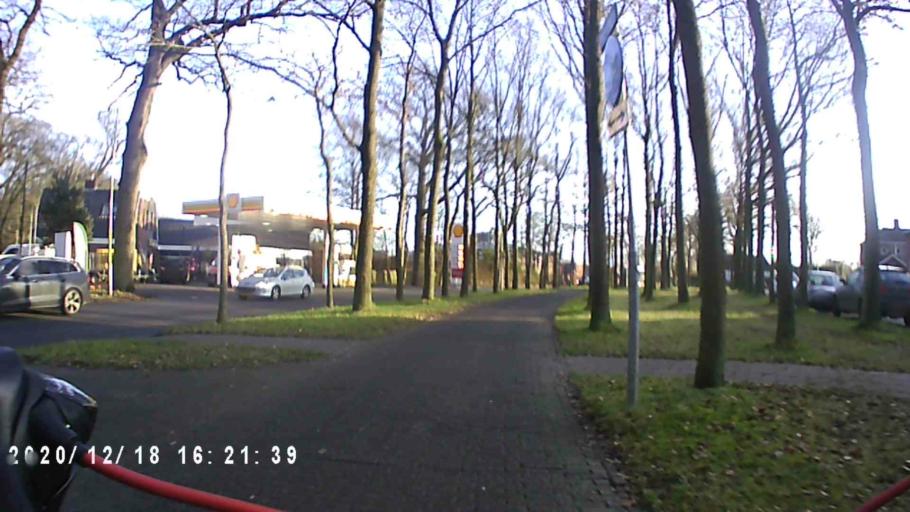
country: NL
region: Drenthe
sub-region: Gemeente Tynaarlo
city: Zuidlaren
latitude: 53.0920
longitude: 6.6899
